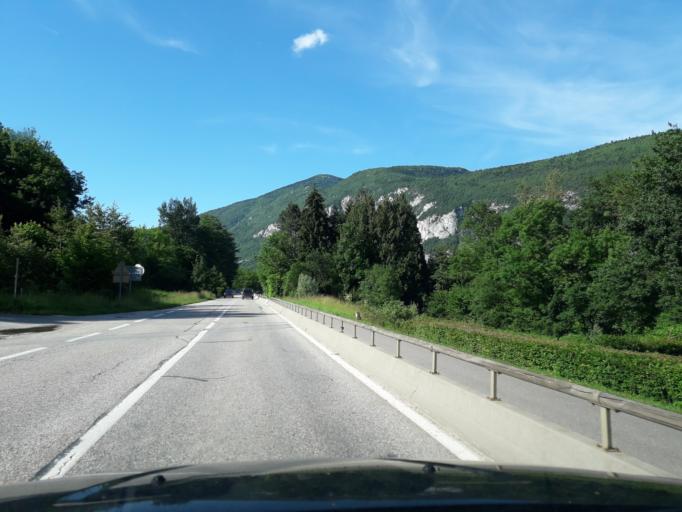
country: FR
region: Rhone-Alpes
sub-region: Departement de la Savoie
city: Novalaise
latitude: 45.5680
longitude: 5.7941
